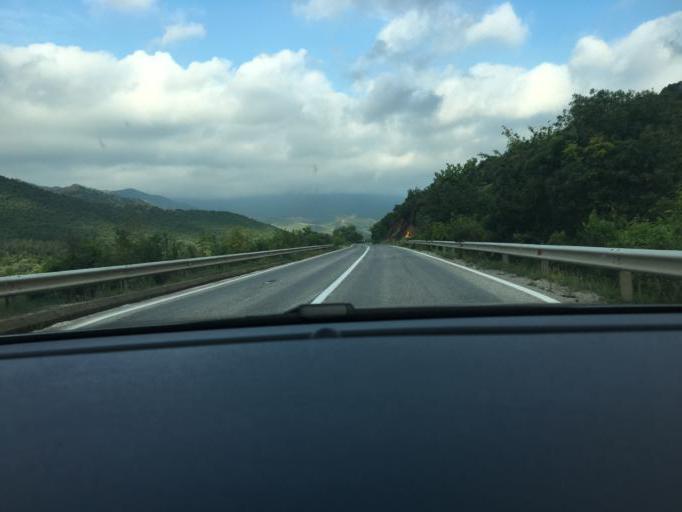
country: MK
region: Demir Kapija
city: Demir Kapija
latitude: 41.3917
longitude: 22.3480
